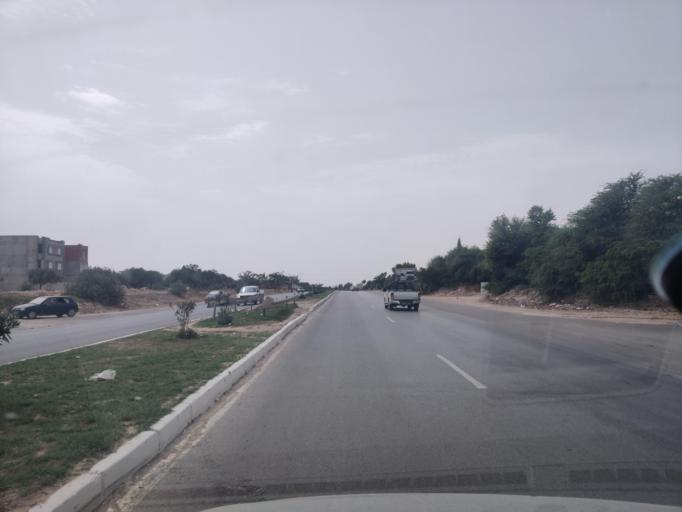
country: TN
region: Susah
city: Hammam Sousse
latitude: 35.8376
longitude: 10.5793
